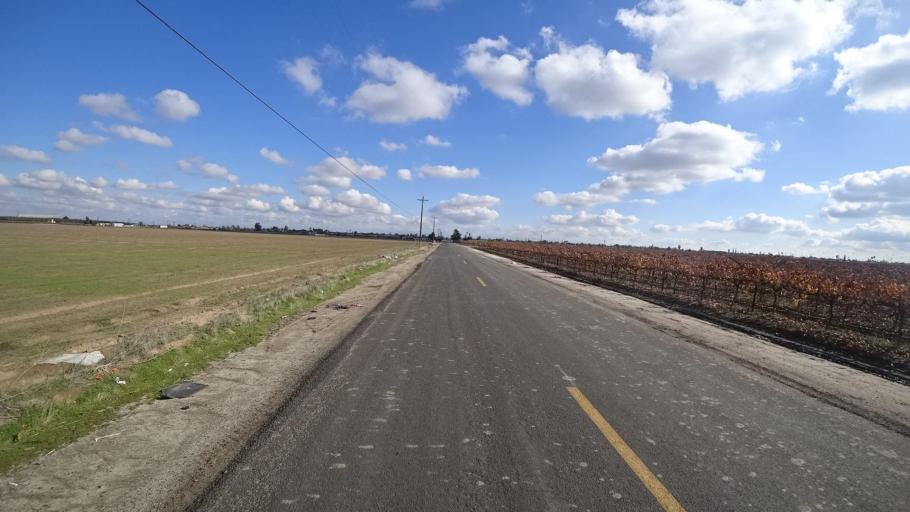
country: US
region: California
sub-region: Kern County
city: McFarland
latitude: 35.6816
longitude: -119.2468
